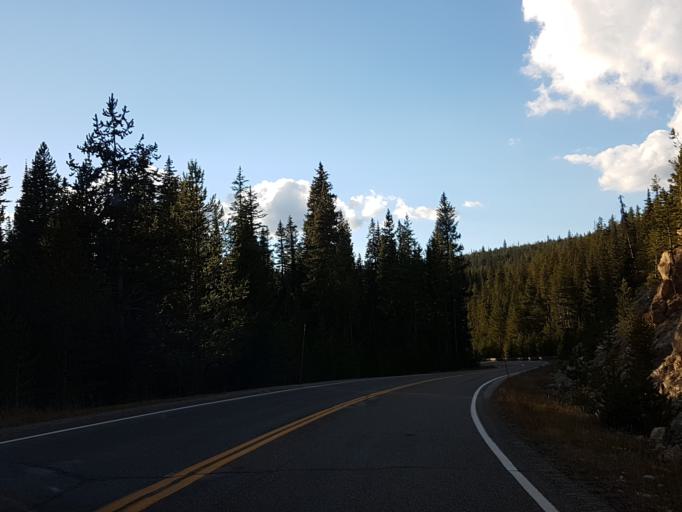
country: US
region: Montana
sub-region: Gallatin County
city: West Yellowstone
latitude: 44.4371
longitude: -110.7278
